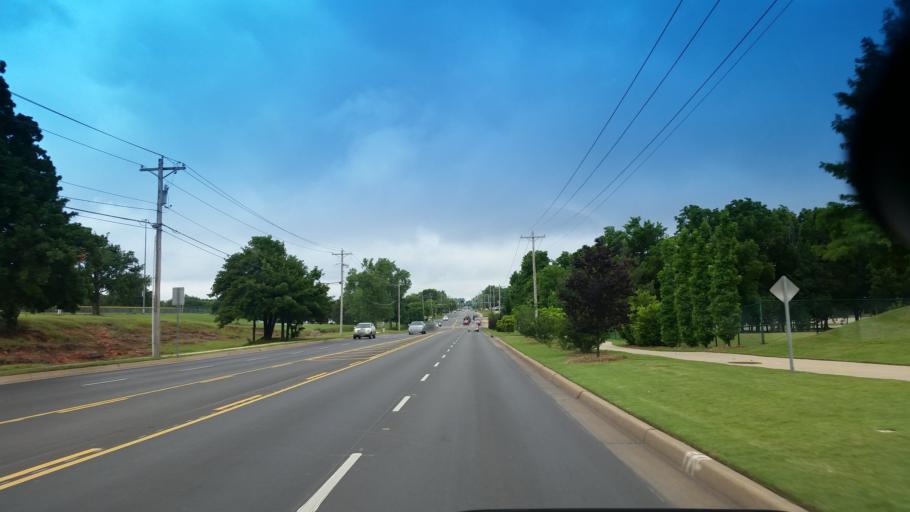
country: US
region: Oklahoma
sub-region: Oklahoma County
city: Edmond
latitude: 35.6484
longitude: -97.4605
